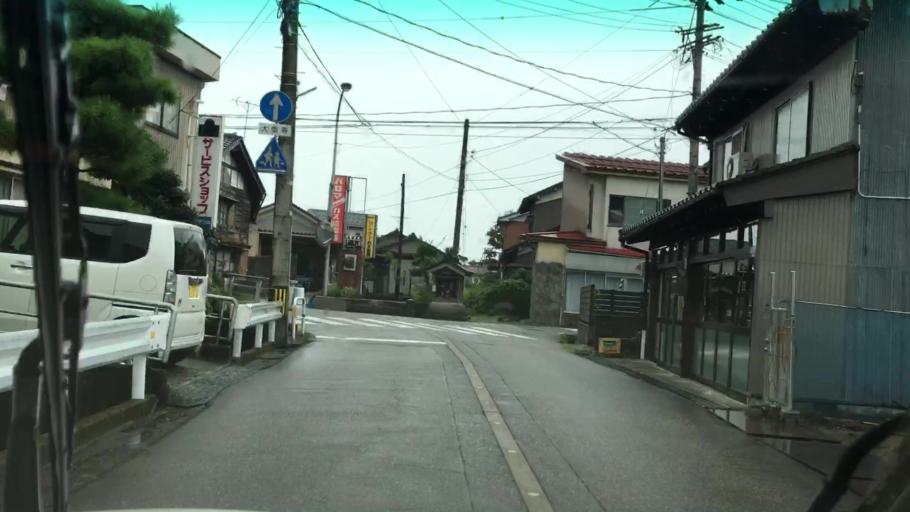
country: JP
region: Toyama
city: Kamiichi
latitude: 36.6571
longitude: 137.3184
